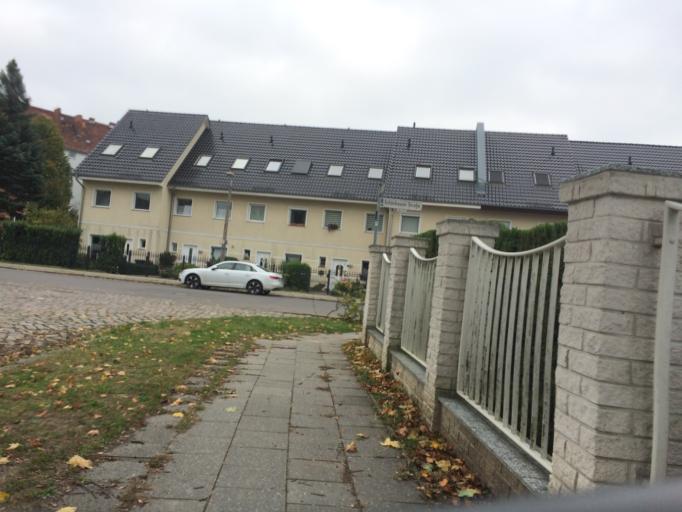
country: DE
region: Berlin
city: Buchholz
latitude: 52.5986
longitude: 13.4276
